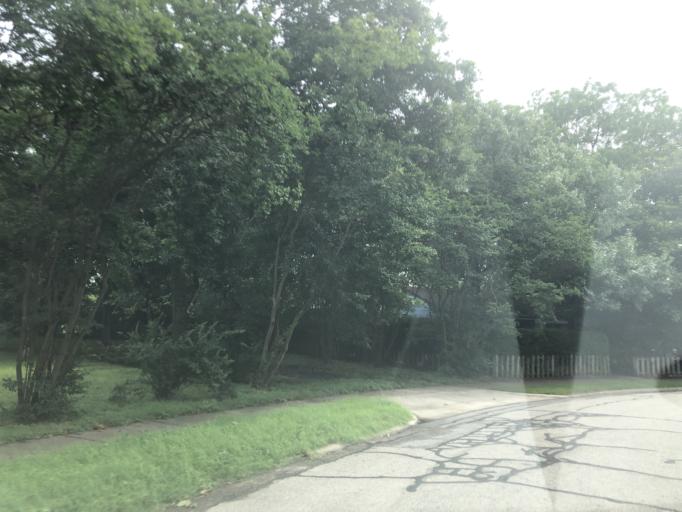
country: US
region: Texas
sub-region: Dallas County
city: Irving
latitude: 32.8061
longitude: -96.9517
